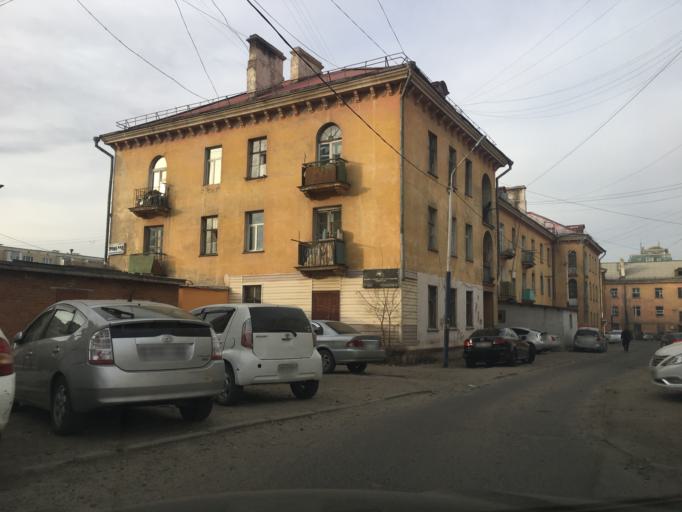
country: MN
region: Ulaanbaatar
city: Ulaanbaatar
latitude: 47.9151
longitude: 106.8828
